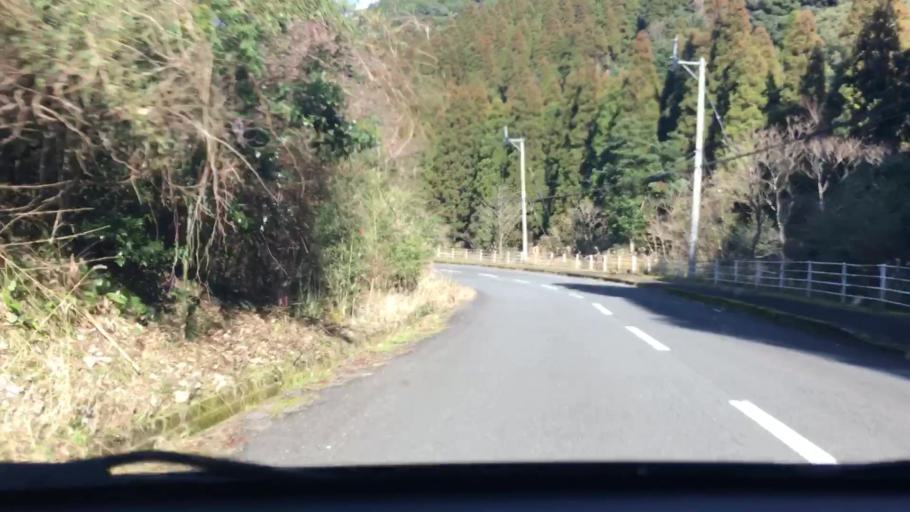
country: JP
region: Kagoshima
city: Satsumasendai
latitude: 31.7496
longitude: 130.4107
